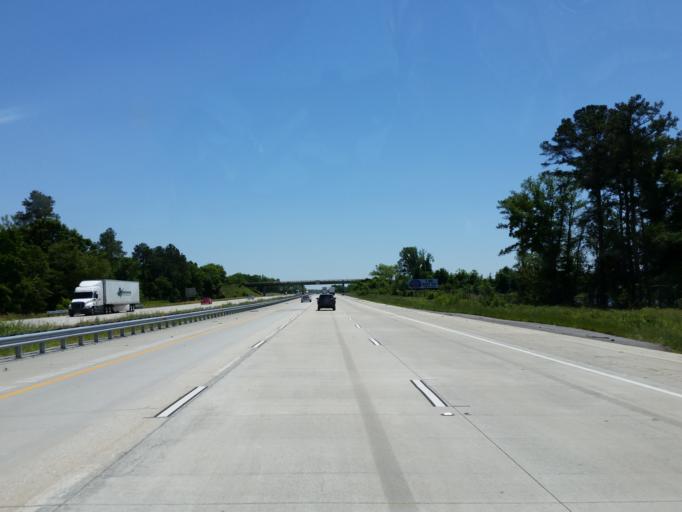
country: US
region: Georgia
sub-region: Dooly County
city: Vienna
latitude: 32.0631
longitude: -83.7637
